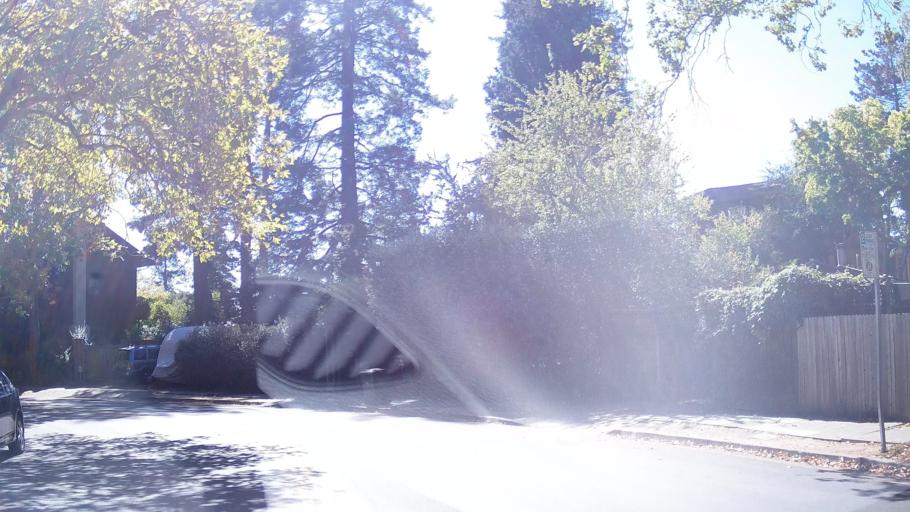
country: US
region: California
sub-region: Alameda County
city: Berkeley
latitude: 37.8876
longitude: -122.2624
